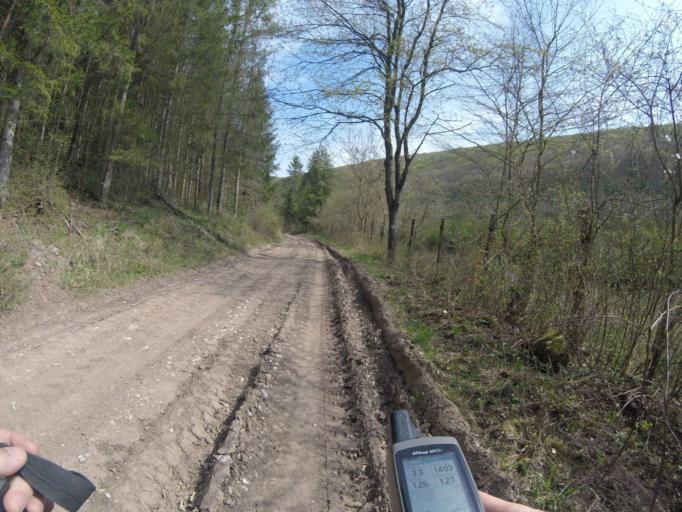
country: HU
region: Borsod-Abauj-Zemplen
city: Rudabanya
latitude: 48.5305
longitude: 20.6290
